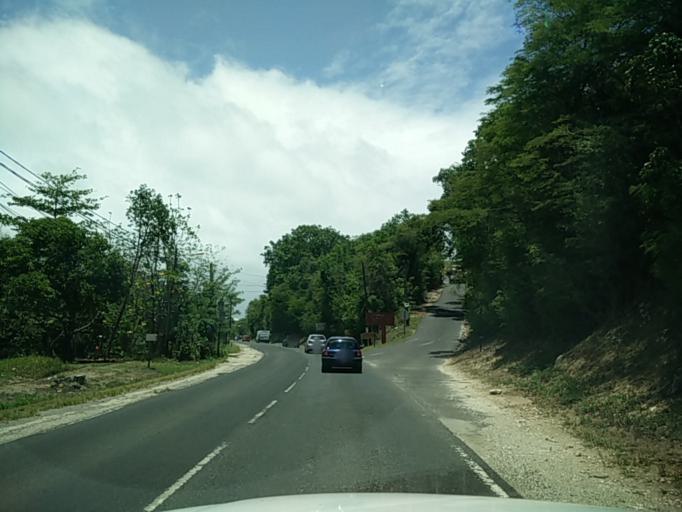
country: GP
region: Guadeloupe
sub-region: Guadeloupe
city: Sainte-Anne
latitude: 16.2193
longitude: -61.4061
